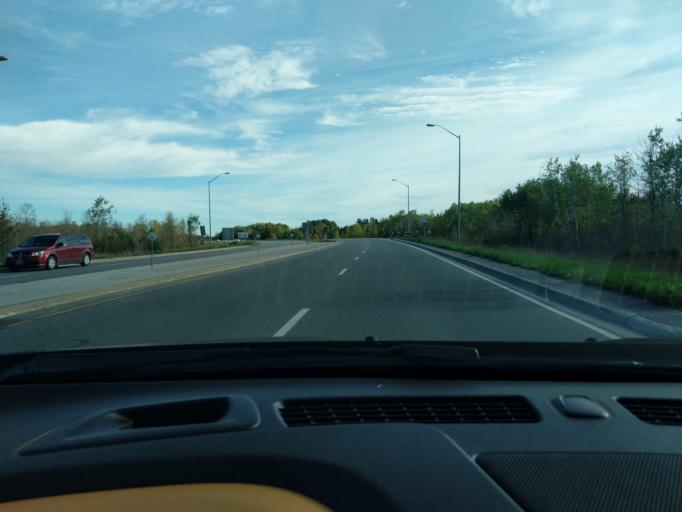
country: CA
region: Ontario
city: Collingwood
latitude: 44.4855
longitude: -80.1731
